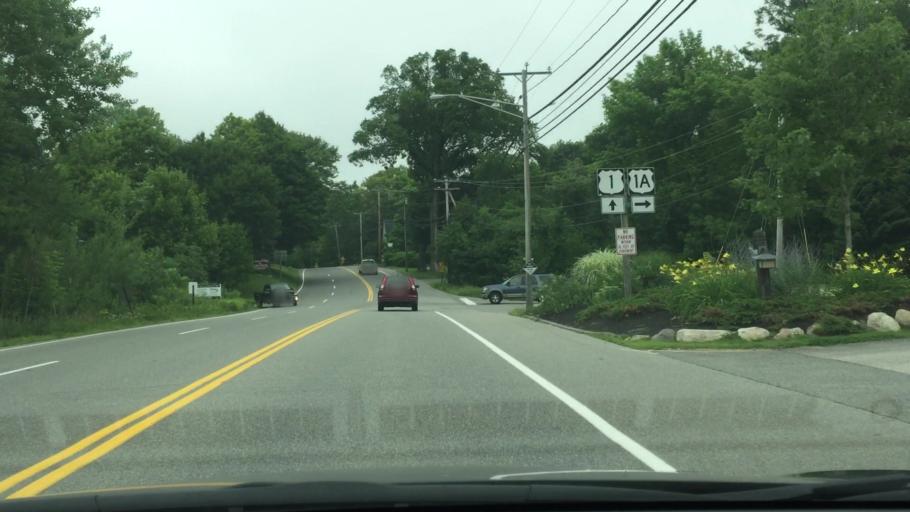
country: US
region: Maine
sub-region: York County
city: Cape Neddick
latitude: 43.1904
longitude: -70.6200
